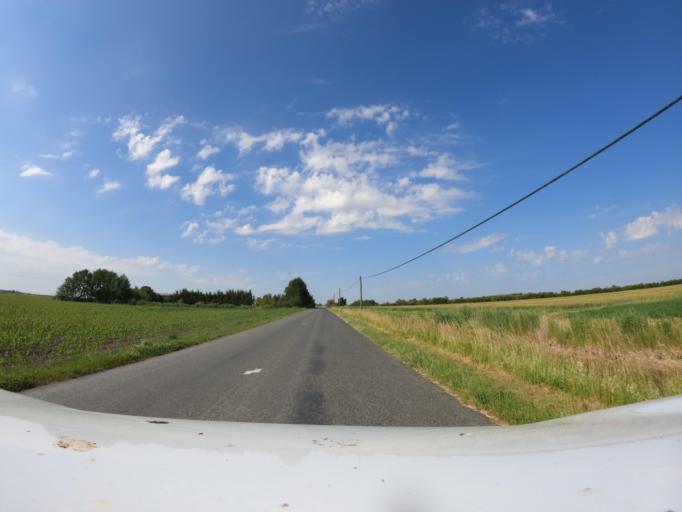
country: FR
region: Pays de la Loire
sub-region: Departement de la Vendee
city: Champagne-les-Marais
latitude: 46.3576
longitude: -1.1162
